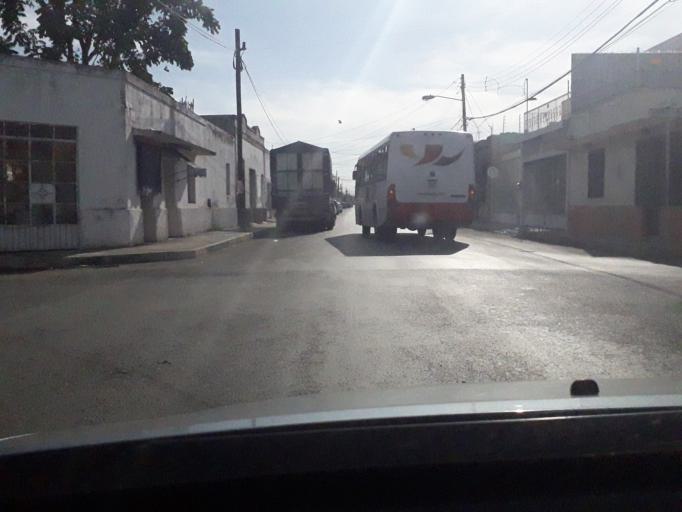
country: MX
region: Yucatan
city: Merida
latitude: 20.9611
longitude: -89.6142
